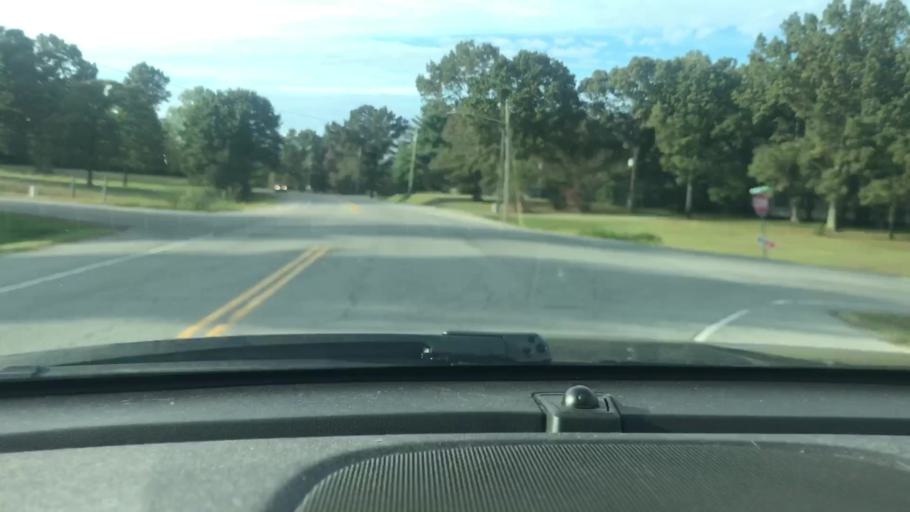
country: US
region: Tennessee
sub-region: Dickson County
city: White Bluff
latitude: 36.1270
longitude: -87.2279
